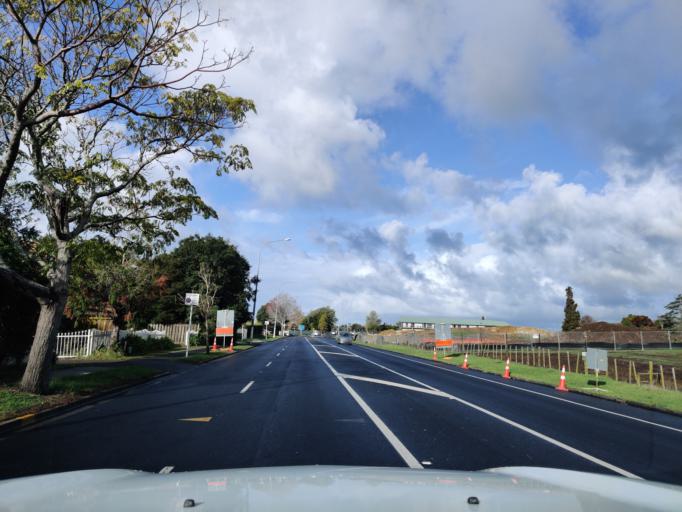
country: NZ
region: Auckland
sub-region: Auckland
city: Pakuranga
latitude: -36.9153
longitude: 174.9113
